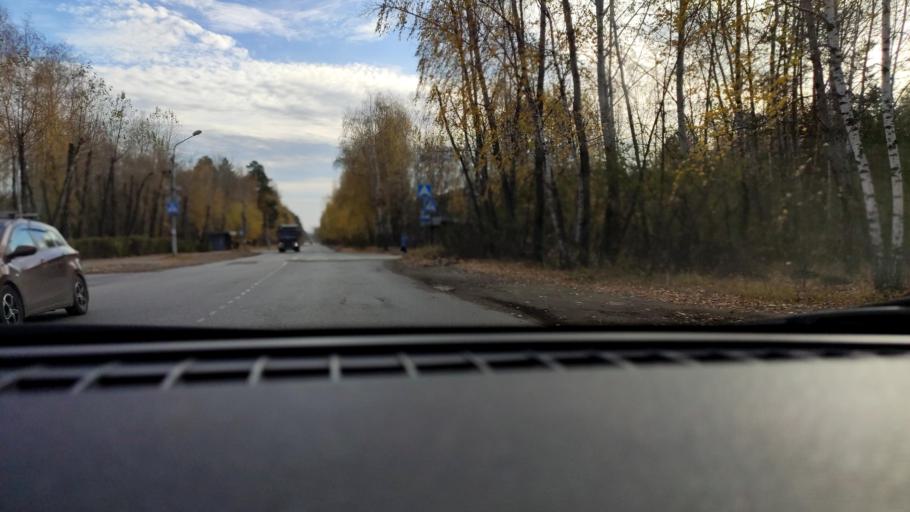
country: RU
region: Perm
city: Overyata
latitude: 58.0146
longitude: 55.9053
